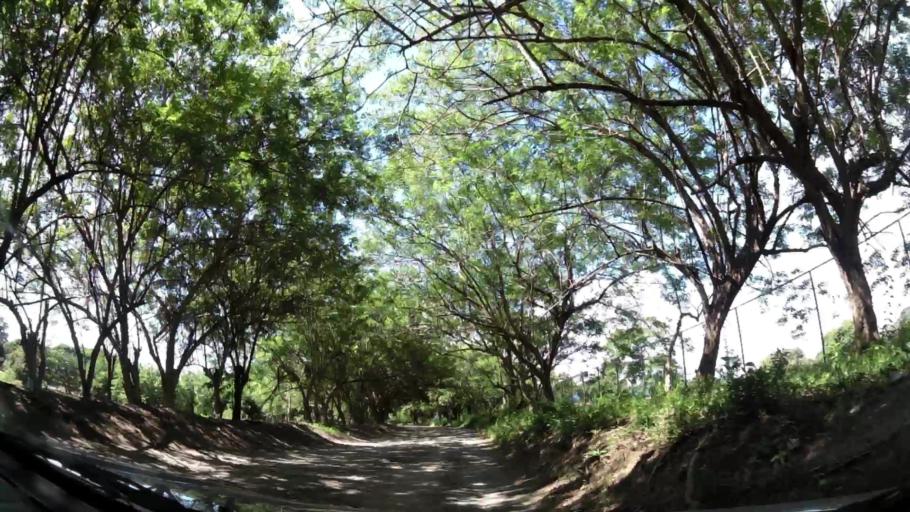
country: PA
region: Panama
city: Nueva Gorgona
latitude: 8.5571
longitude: -79.8600
